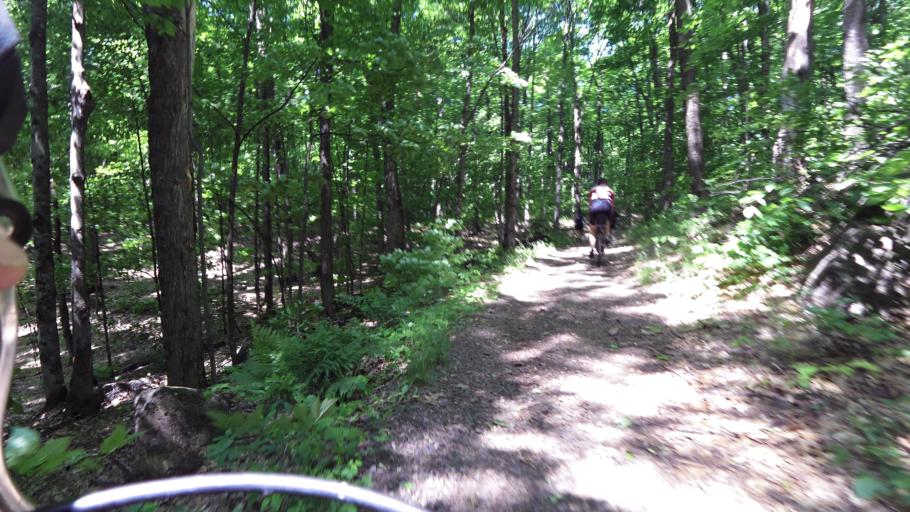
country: CA
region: Quebec
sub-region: Outaouais
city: Wakefield
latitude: 45.5541
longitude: -75.8966
